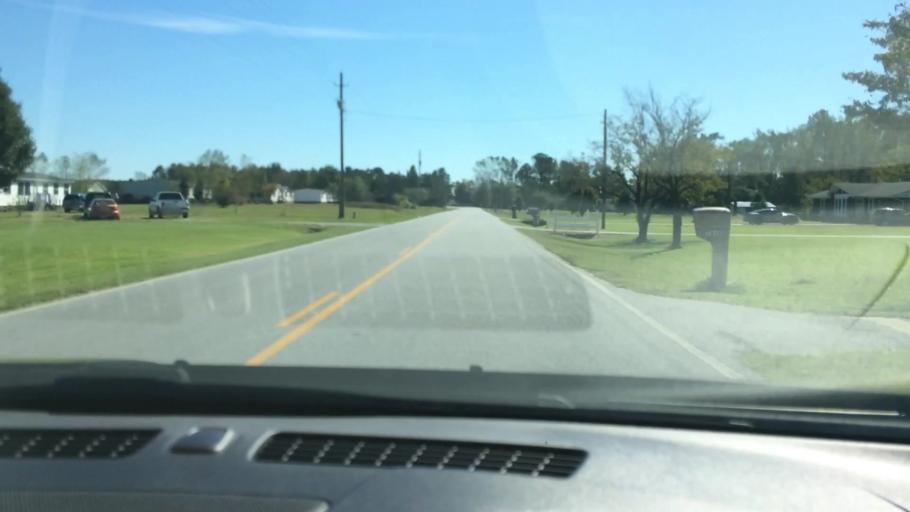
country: US
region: North Carolina
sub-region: Pitt County
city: Grifton
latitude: 35.3798
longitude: -77.3703
